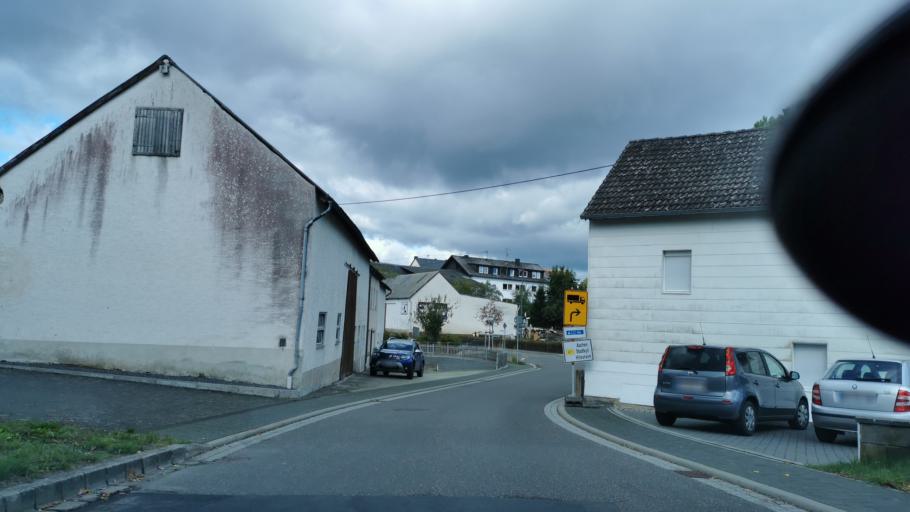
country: DE
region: Rheinland-Pfalz
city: Walsdorf
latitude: 50.2777
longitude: 6.7369
